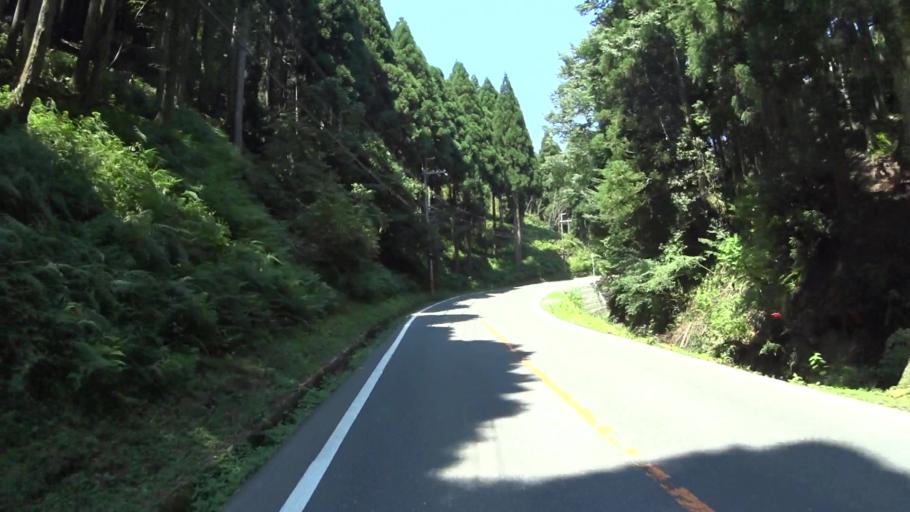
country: JP
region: Fukui
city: Obama
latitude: 35.4054
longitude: 135.9339
